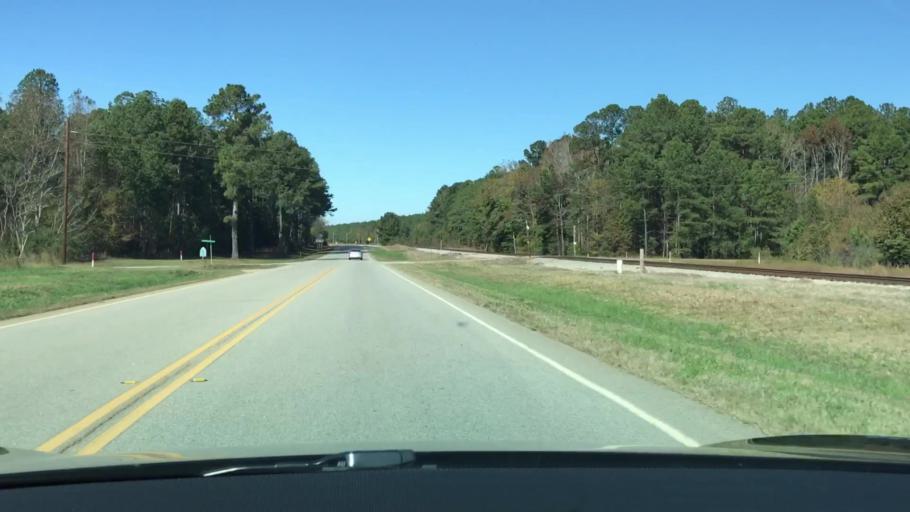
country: US
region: Georgia
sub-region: Warren County
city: Firing Range
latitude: 33.4744
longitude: -82.7273
